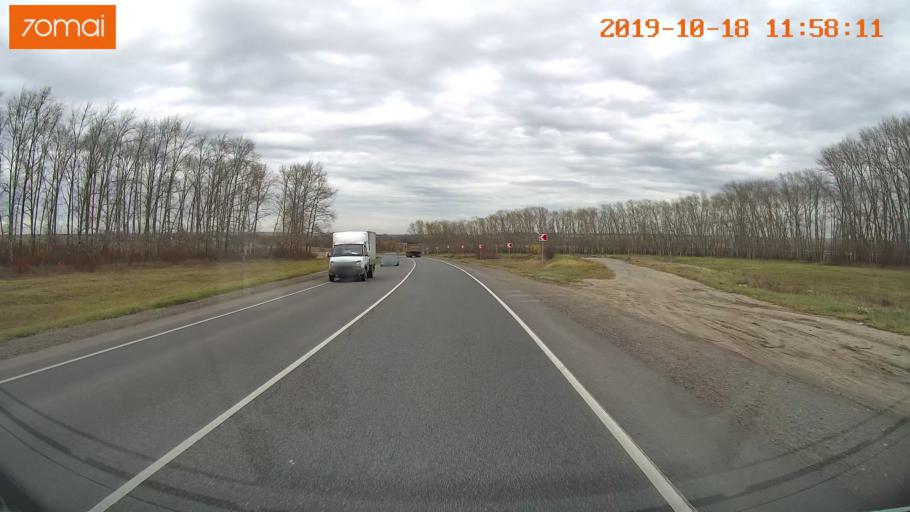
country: RU
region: Rjazan
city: Mikhaylov
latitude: 54.2692
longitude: 39.1630
